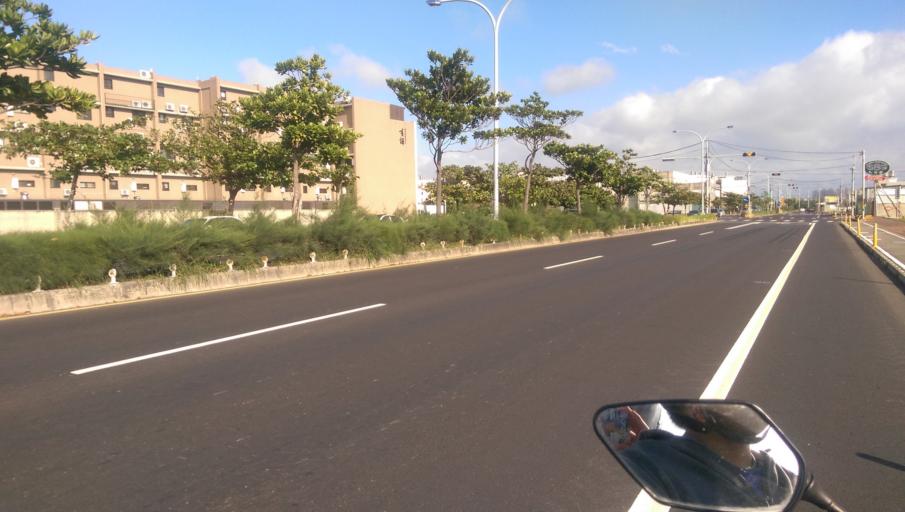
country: TW
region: Taiwan
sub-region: Hsinchu
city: Hsinchu
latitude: 24.8353
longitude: 120.9414
